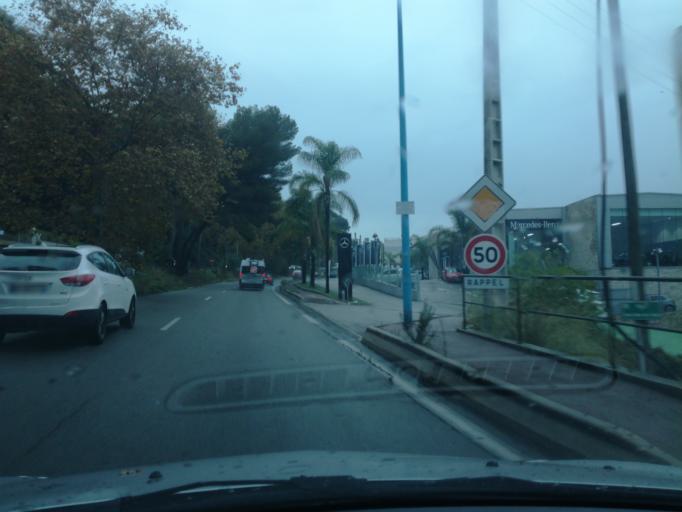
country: FR
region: Provence-Alpes-Cote d'Azur
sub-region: Departement des Alpes-Maritimes
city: Le Cannet
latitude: 43.5729
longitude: 7.0129
